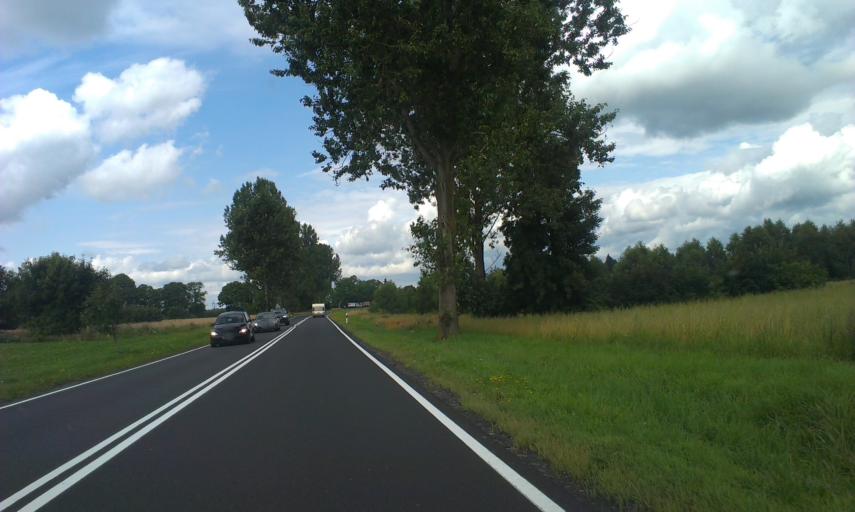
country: PL
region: West Pomeranian Voivodeship
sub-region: Powiat koszalinski
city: Bobolice
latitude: 54.0238
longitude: 16.4716
